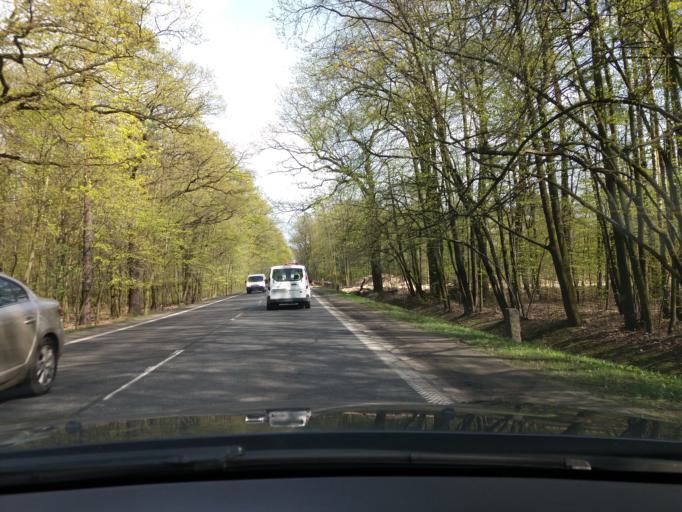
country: PL
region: Lower Silesian Voivodeship
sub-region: Powiat sredzki
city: Mrozow
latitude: 51.1488
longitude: 16.8418
